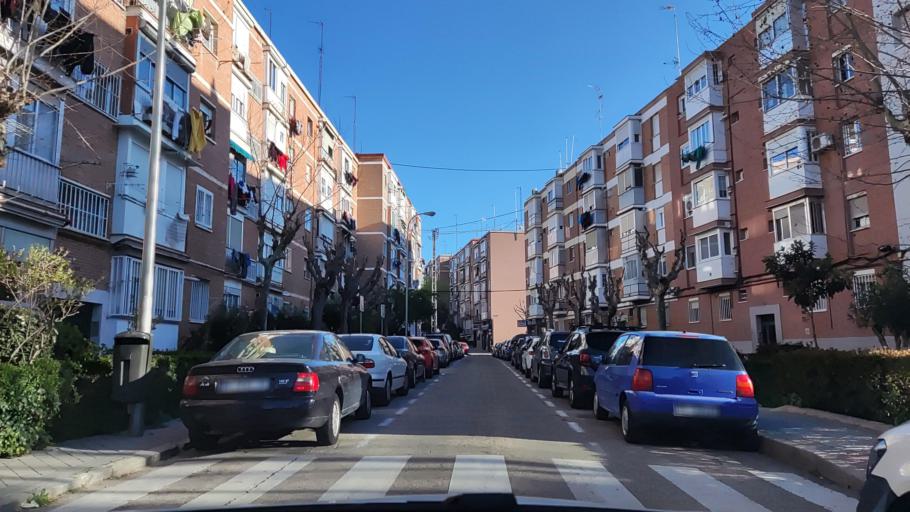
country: ES
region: Madrid
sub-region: Provincia de Madrid
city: Latina
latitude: 40.3991
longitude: -3.7736
